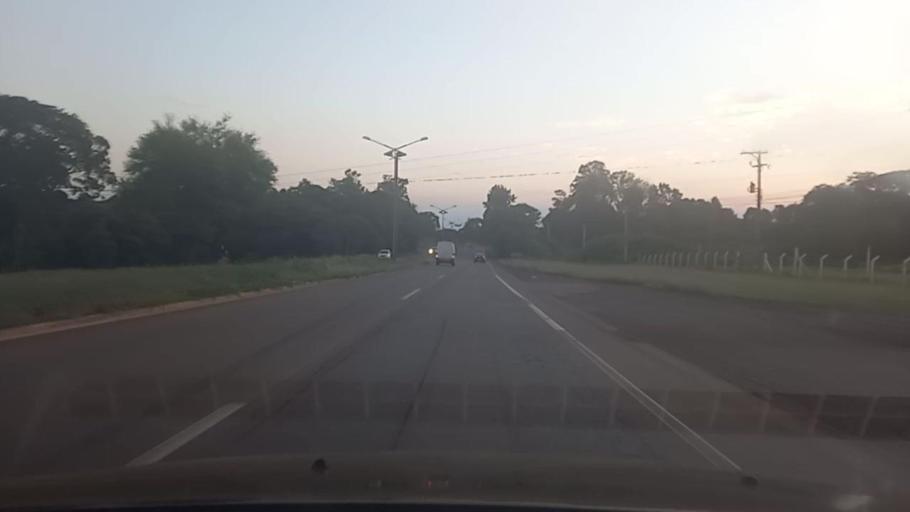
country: BR
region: Rio Grande do Sul
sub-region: Passo Fundo
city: Passo Fundo
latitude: -28.2823
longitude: -52.4520
